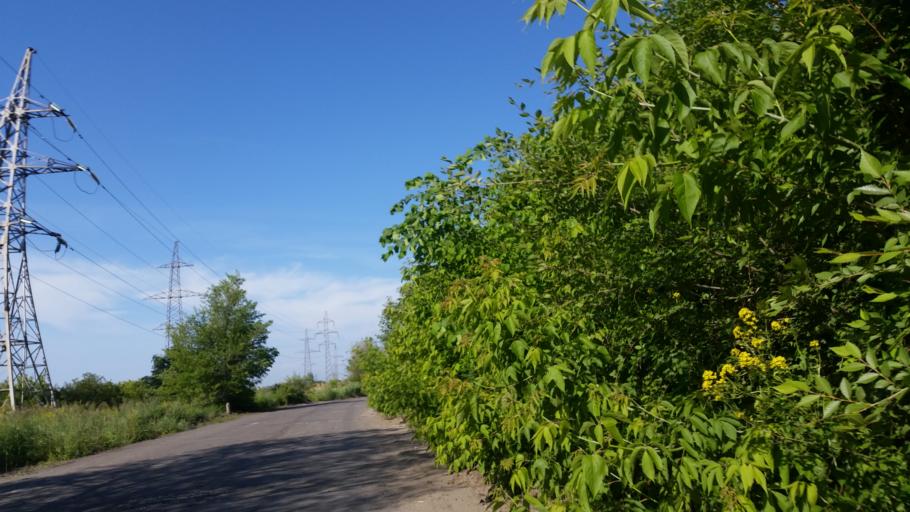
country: RU
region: Ulyanovsk
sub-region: Ulyanovskiy Rayon
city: Ulyanovsk
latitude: 54.3063
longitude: 48.4064
